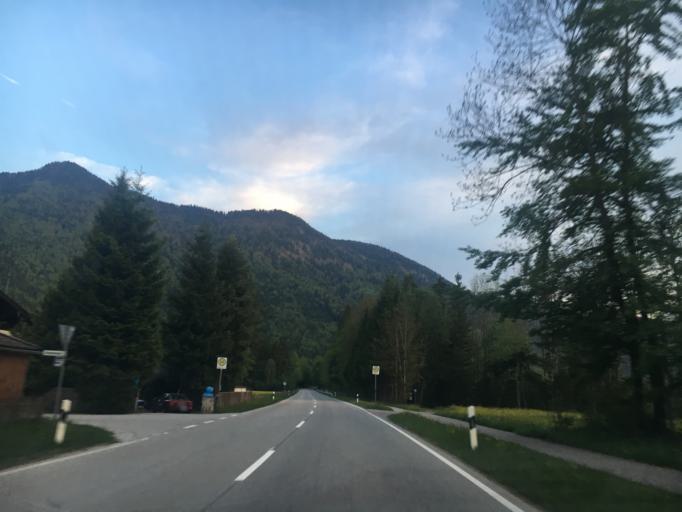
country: DE
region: Bavaria
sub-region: Upper Bavaria
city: Lenggries
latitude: 47.6285
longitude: 11.5943
